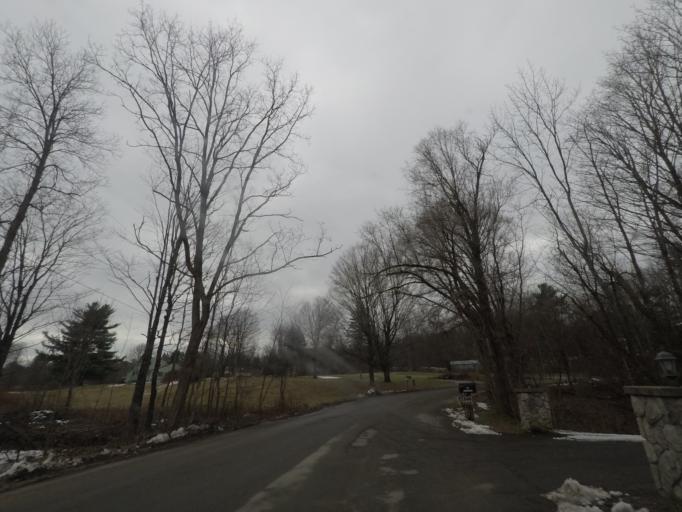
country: US
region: New York
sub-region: Rensselaer County
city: East Greenbush
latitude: 42.5906
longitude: -73.6410
